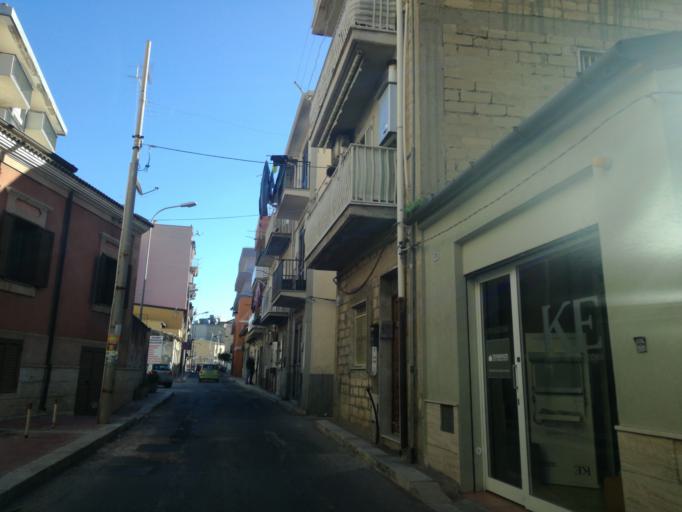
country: IT
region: Sicily
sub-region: Provincia di Caltanissetta
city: Gela
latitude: 37.0713
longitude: 14.2353
